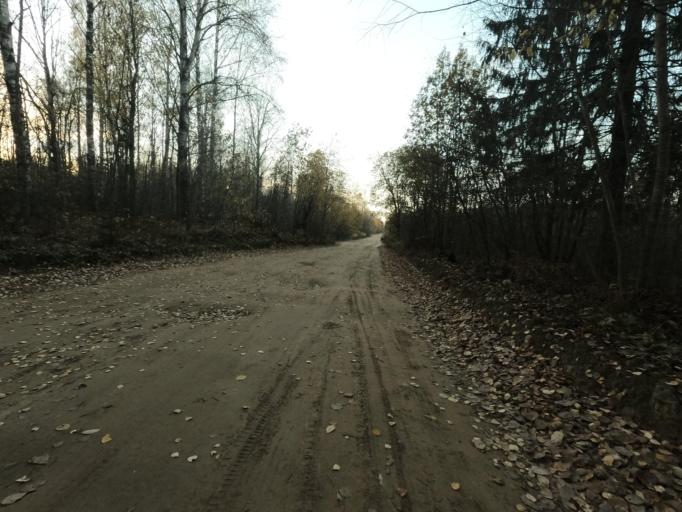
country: RU
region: Leningrad
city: Mga
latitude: 59.7555
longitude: 31.2785
